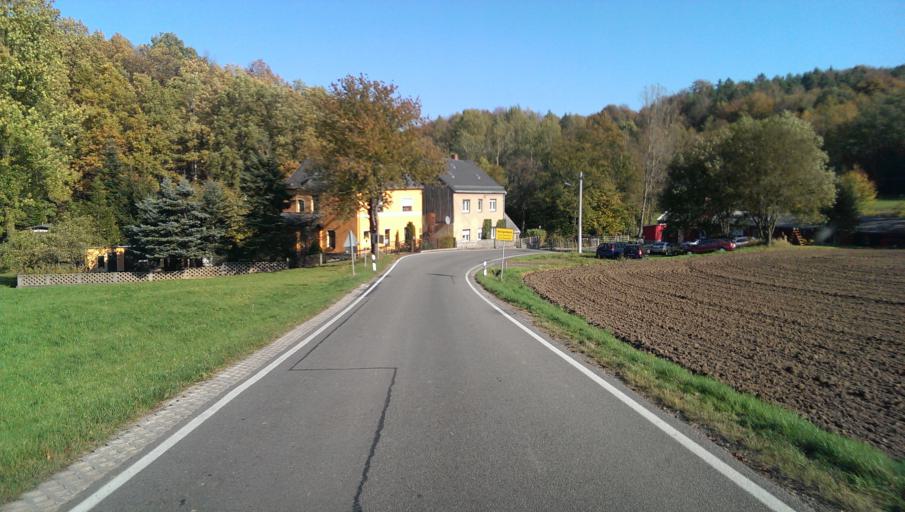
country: DE
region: Saxony
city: Kriebstein
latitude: 51.0623
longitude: 13.0077
